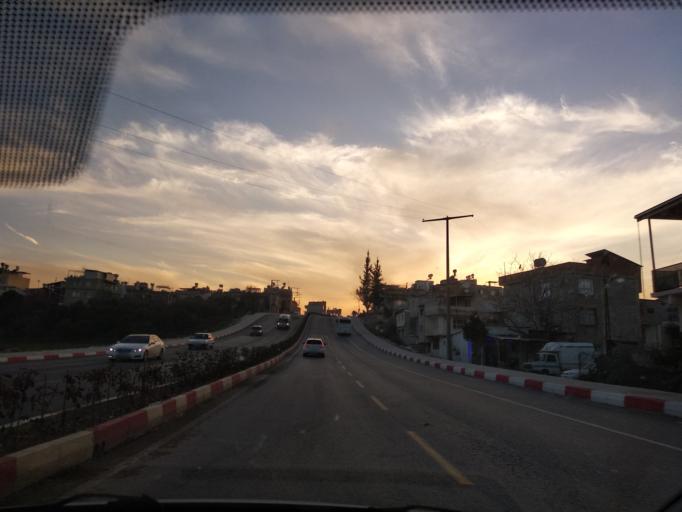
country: TR
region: Mersin
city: Mercin
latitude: 36.8281
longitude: 34.6086
